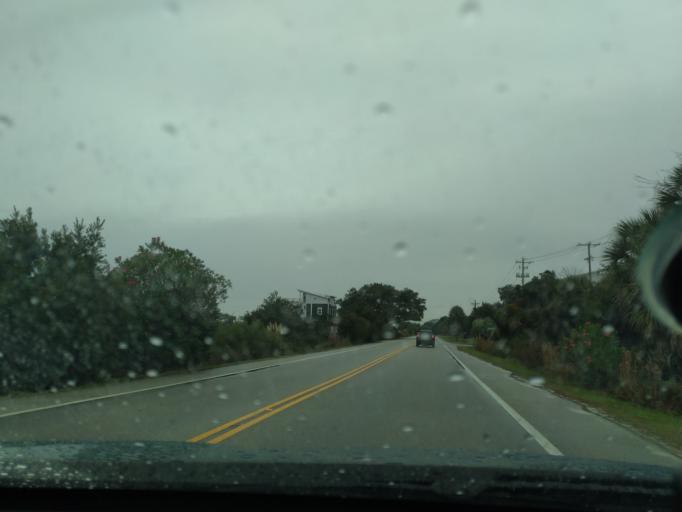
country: US
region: South Carolina
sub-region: Charleston County
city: Folly Beach
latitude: 32.6703
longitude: -79.9475
